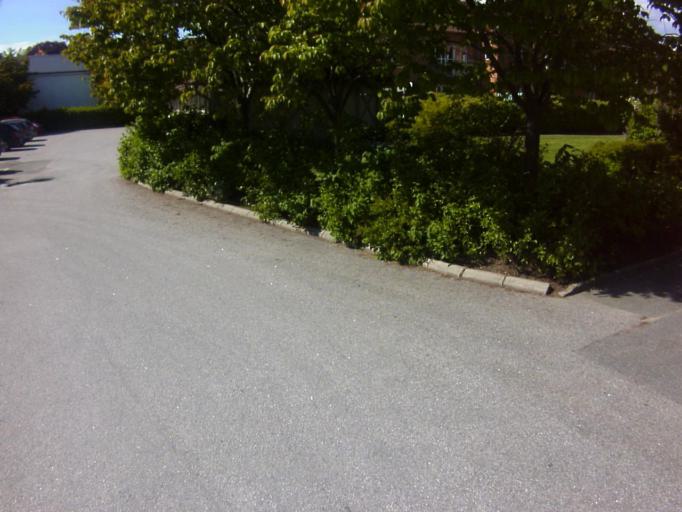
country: SE
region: Blekinge
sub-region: Solvesborgs Kommun
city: Soelvesborg
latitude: 56.0549
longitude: 14.5916
